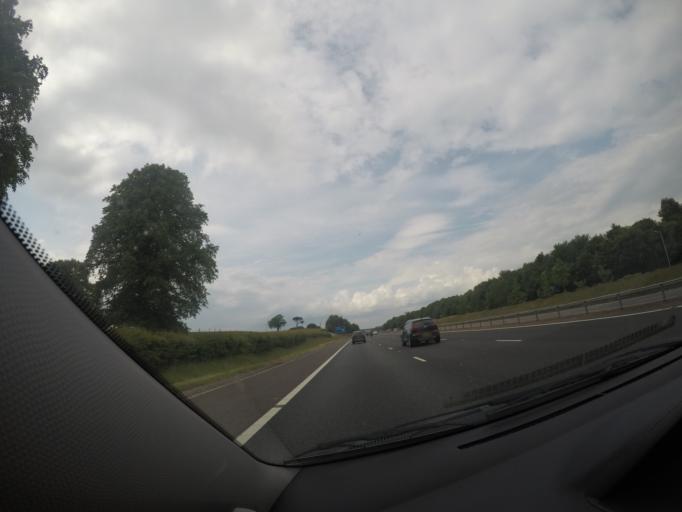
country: GB
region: Scotland
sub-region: Dumfries and Galloway
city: Lockerbie
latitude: 55.1196
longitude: -3.3625
